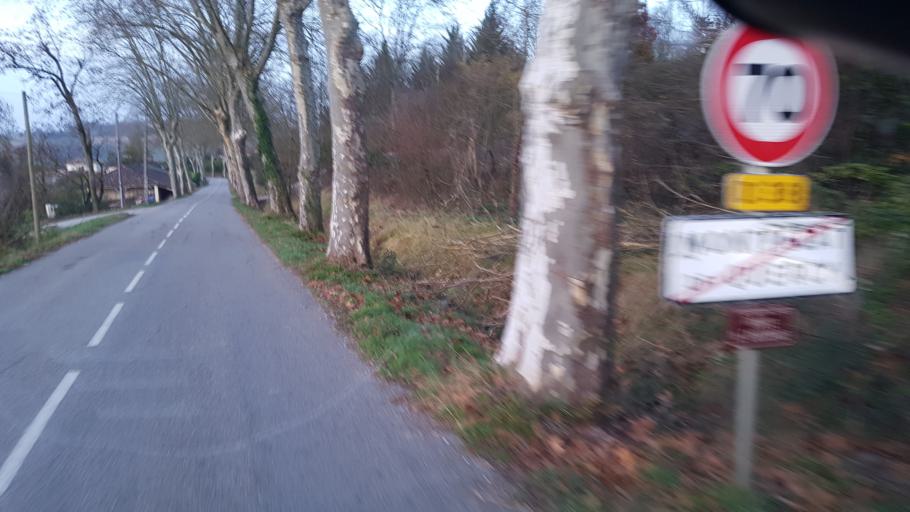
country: FR
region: Midi-Pyrenees
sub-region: Departement du Tarn-et-Garonne
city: Caussade
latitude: 44.2346
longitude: 1.4746
